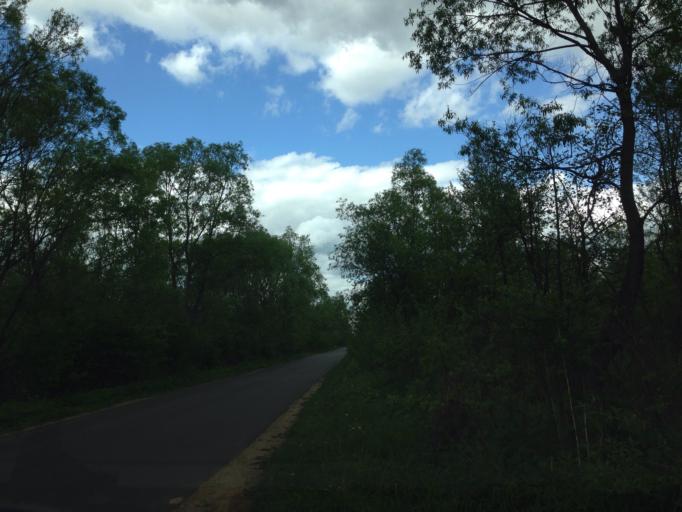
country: PL
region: Podlasie
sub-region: Powiat bialostocki
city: Tykocin
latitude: 53.3146
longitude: 22.6025
